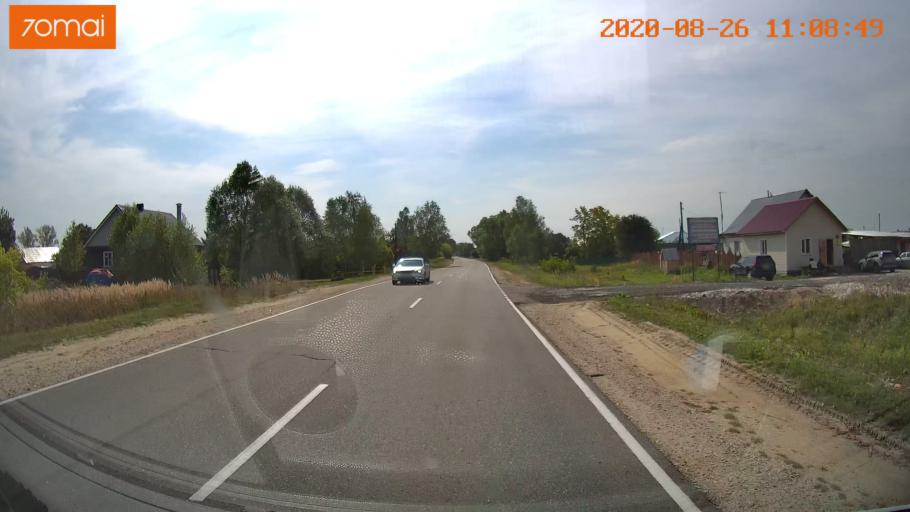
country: RU
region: Rjazan
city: Izhevskoye
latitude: 54.4987
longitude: 41.1228
